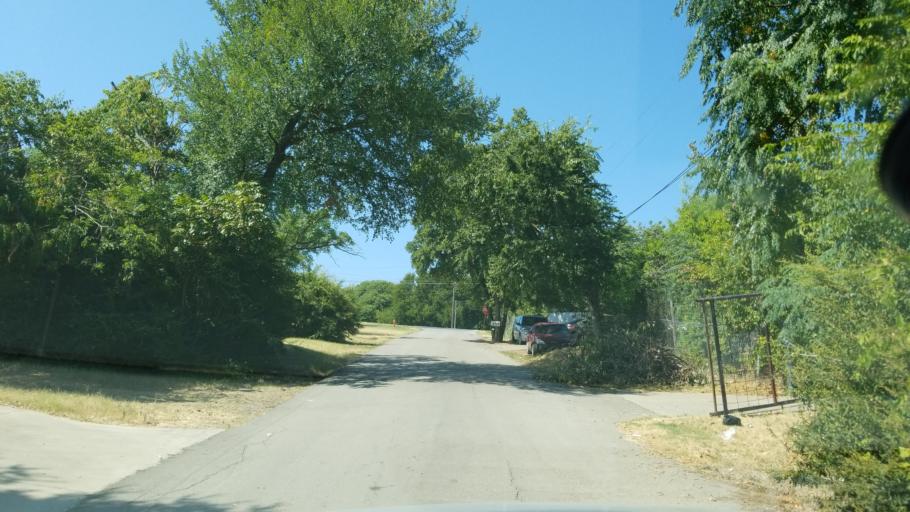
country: US
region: Texas
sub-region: Dallas County
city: Cockrell Hill
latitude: 32.7440
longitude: -96.9035
